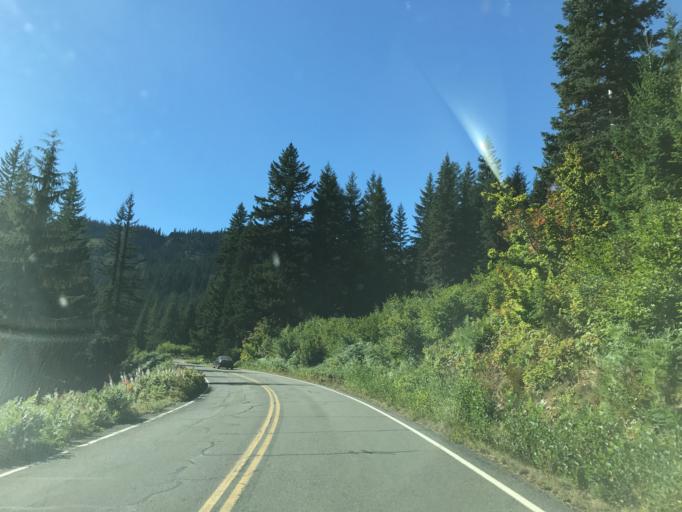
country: US
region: Washington
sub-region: Pierce County
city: Buckley
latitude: 46.7749
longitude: -121.6979
